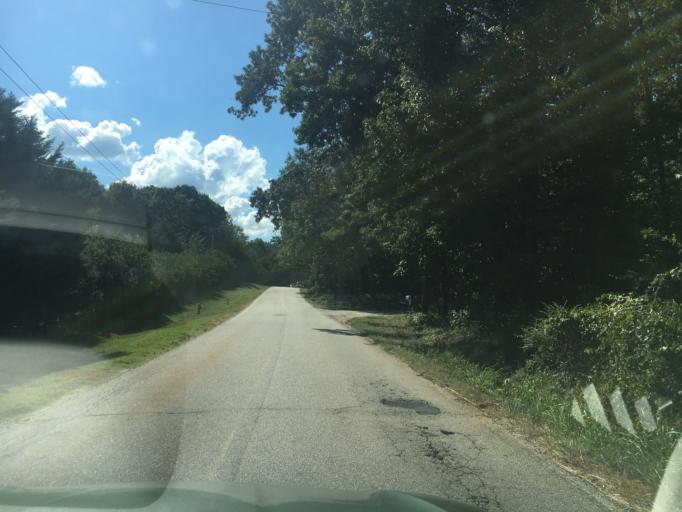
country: US
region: South Carolina
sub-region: Greenville County
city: Five Forks
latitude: 34.8185
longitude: -82.2137
